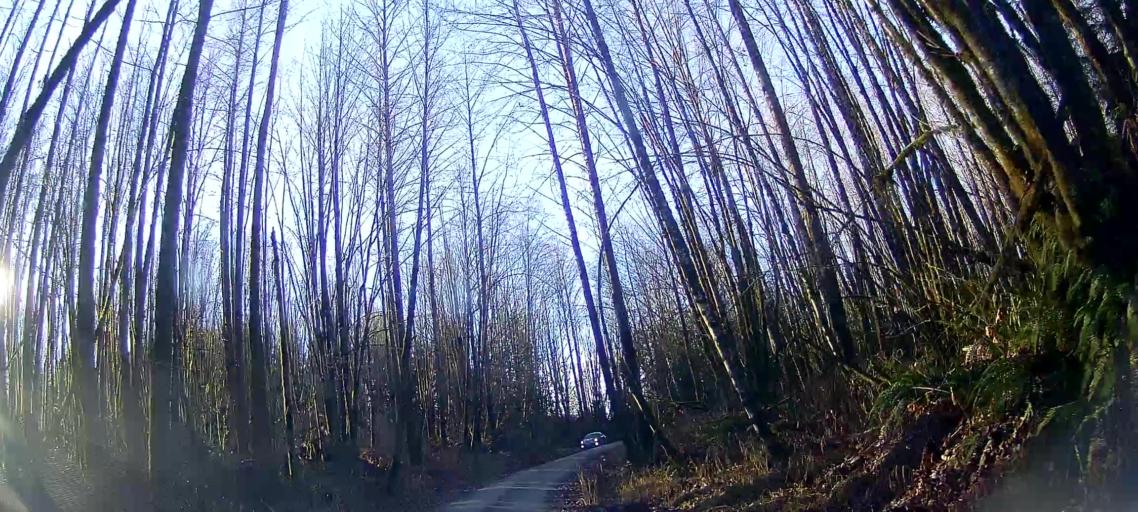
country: US
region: Washington
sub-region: Snohomish County
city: Darrington
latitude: 48.5411
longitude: -121.7320
